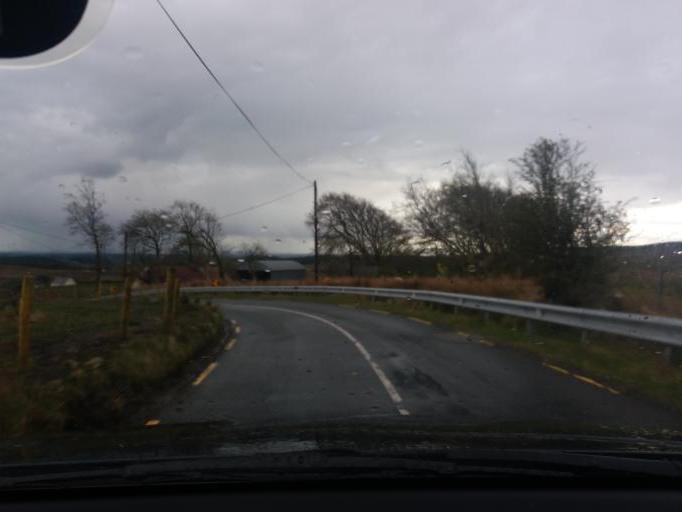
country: IE
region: Ulster
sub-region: An Cabhan
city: Ballyconnell
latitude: 54.1587
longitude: -7.7812
